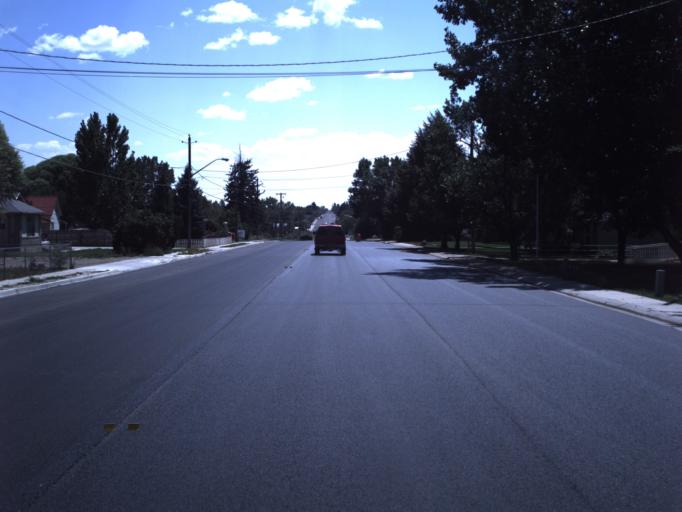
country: US
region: Utah
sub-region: Emery County
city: Orangeville
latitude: 39.2349
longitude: -111.0533
